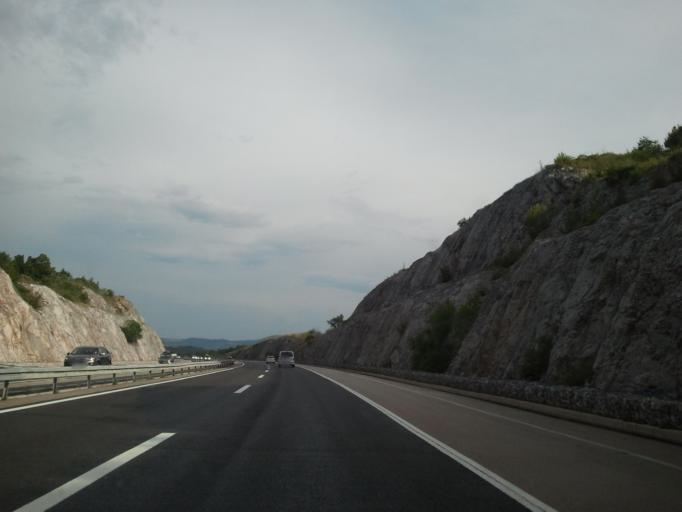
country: HR
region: Zadarska
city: Obrovac
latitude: 44.3370
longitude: 15.6520
